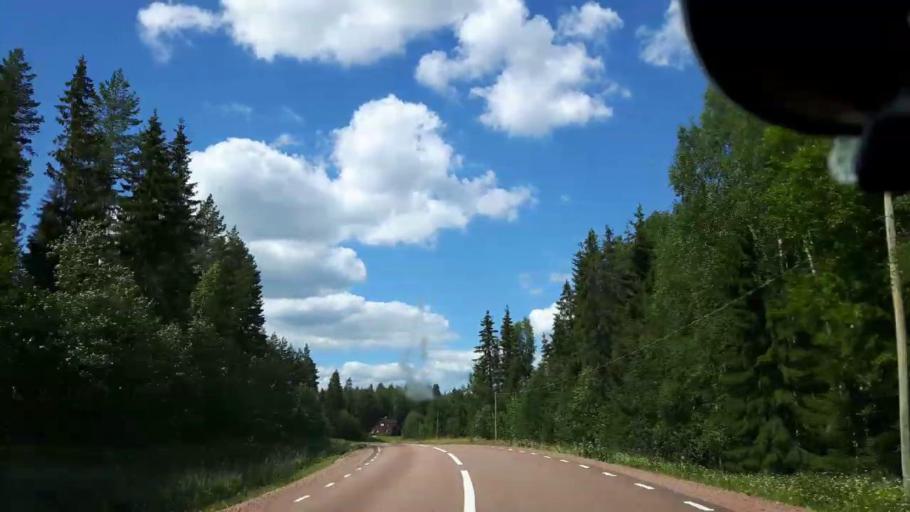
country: SE
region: Jaemtland
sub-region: Ragunda Kommun
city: Hammarstrand
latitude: 63.0253
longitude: 16.5342
